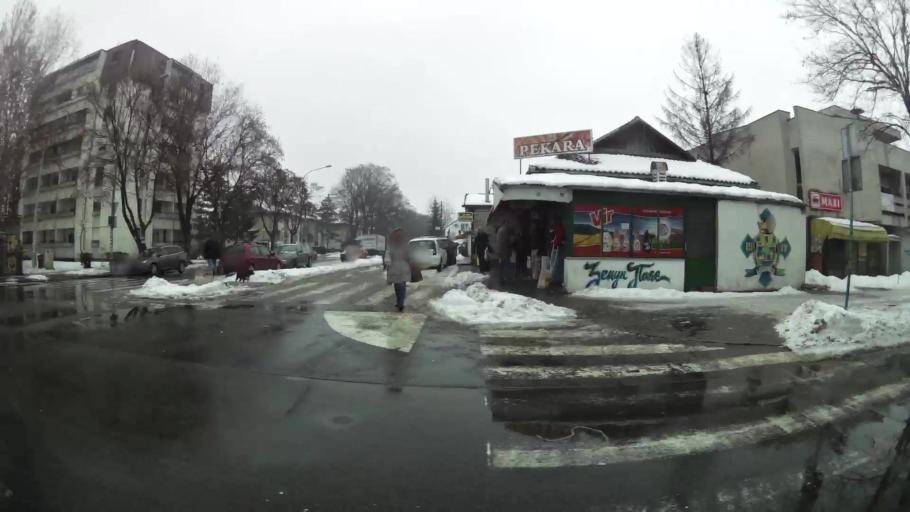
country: RS
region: Central Serbia
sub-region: Belgrade
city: Zemun
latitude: 44.8722
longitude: 20.3241
